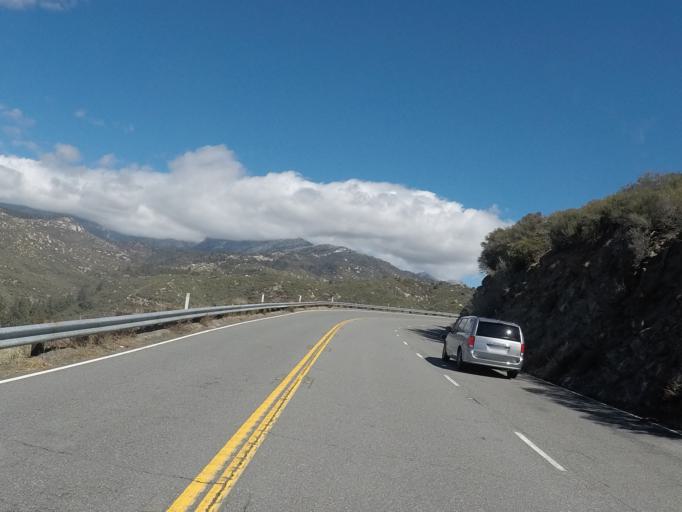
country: US
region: California
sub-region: Riverside County
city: Idyllwild-Pine Cove
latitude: 33.7017
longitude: -116.7475
